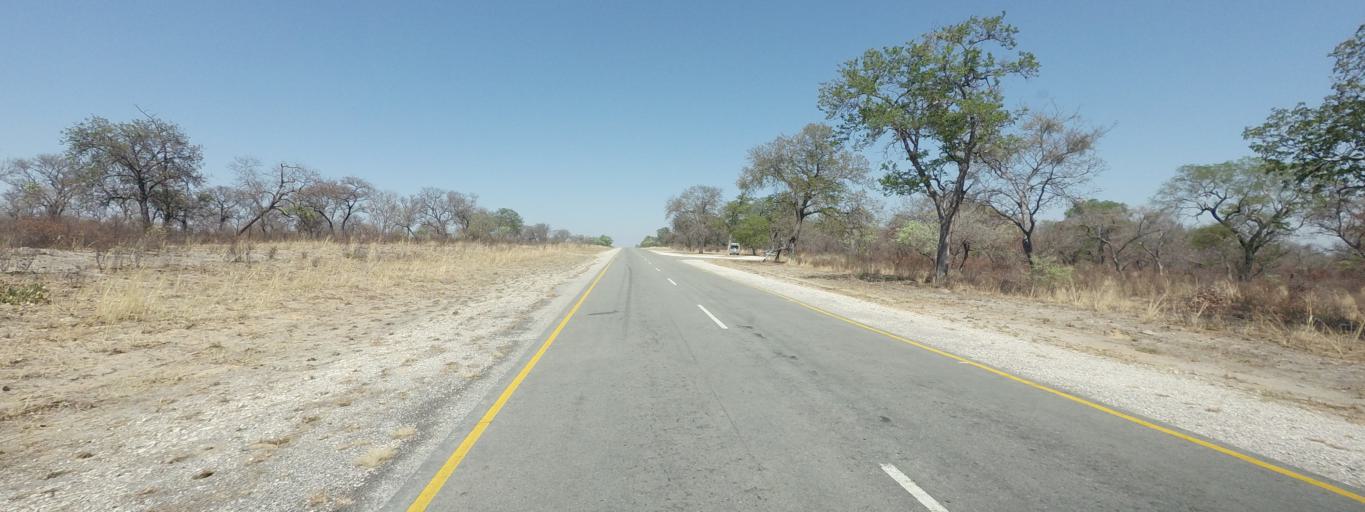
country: BW
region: North West
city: Shakawe
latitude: -17.9510
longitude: 22.5867
